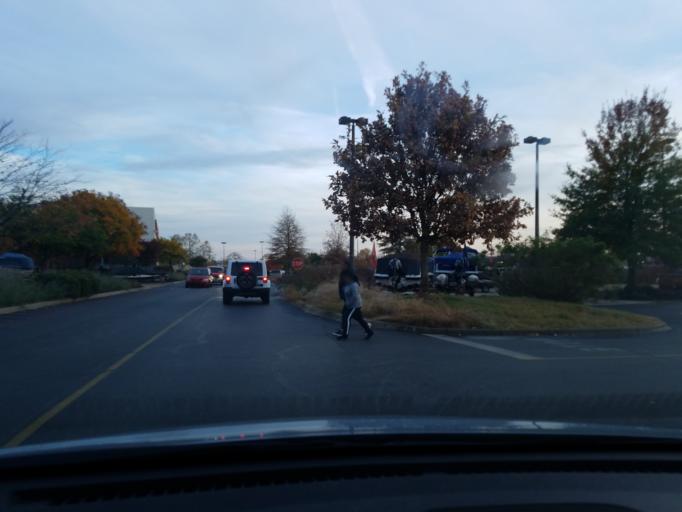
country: US
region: Indiana
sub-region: Clark County
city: Clarksville
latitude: 38.3206
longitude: -85.7631
